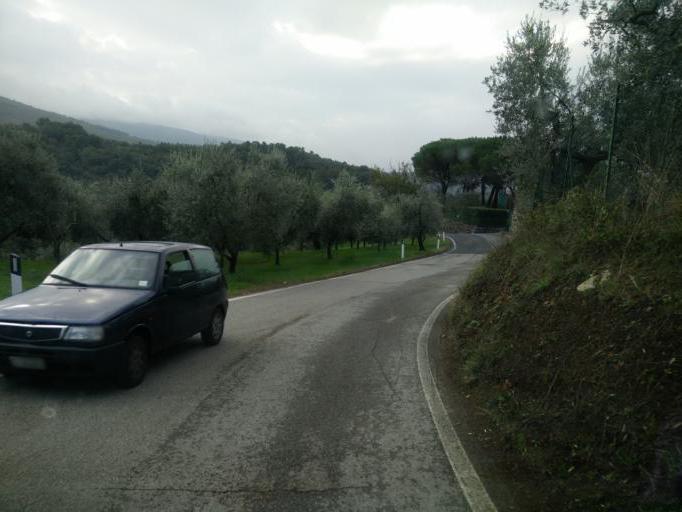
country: IT
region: Tuscany
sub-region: Provincia di Prato
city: Vaiano
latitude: 43.9337
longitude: 11.0946
